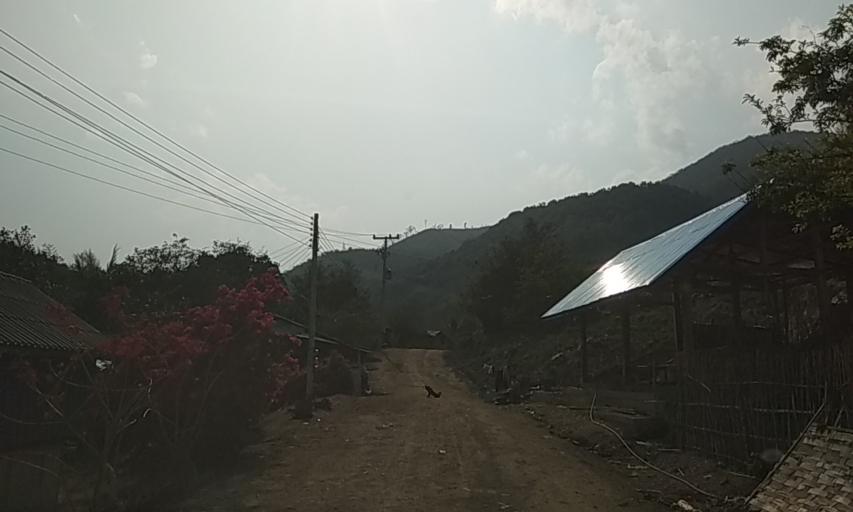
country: LA
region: Louangphabang
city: Louangphabang
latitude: 20.0526
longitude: 101.8544
